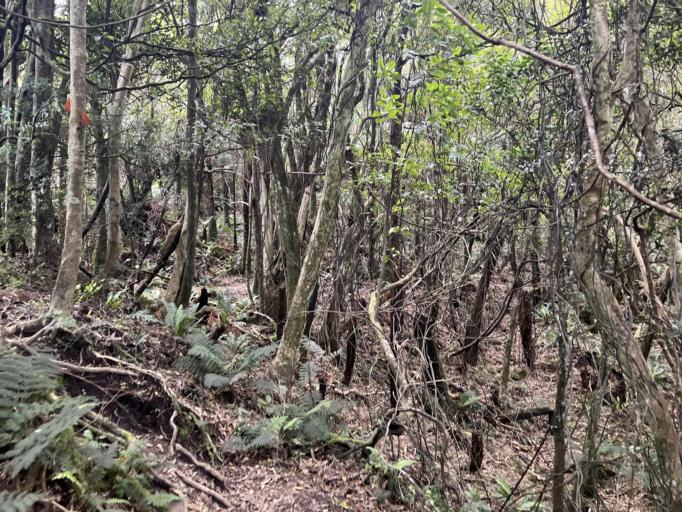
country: NZ
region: Wellington
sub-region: Kapiti Coast District
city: Paraparaumu
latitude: -40.8783
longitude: 175.0912
